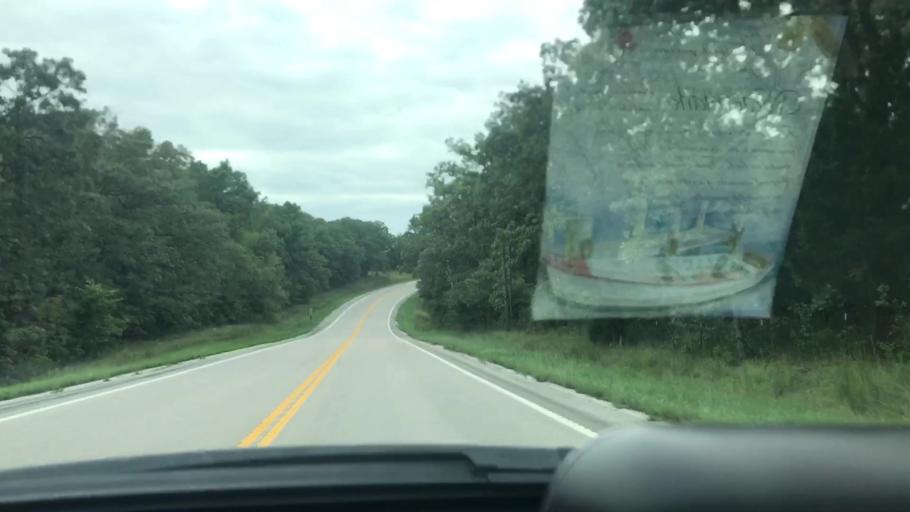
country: US
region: Missouri
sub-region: Benton County
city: Warsaw
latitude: 38.1623
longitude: -93.3017
